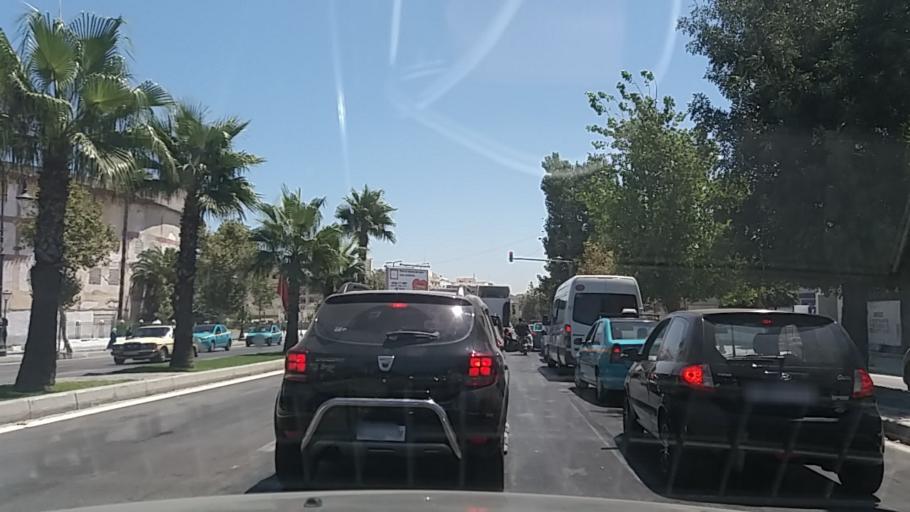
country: MA
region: Tanger-Tetouan
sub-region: Tanger-Assilah
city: Tangier
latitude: 35.7646
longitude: -5.7977
